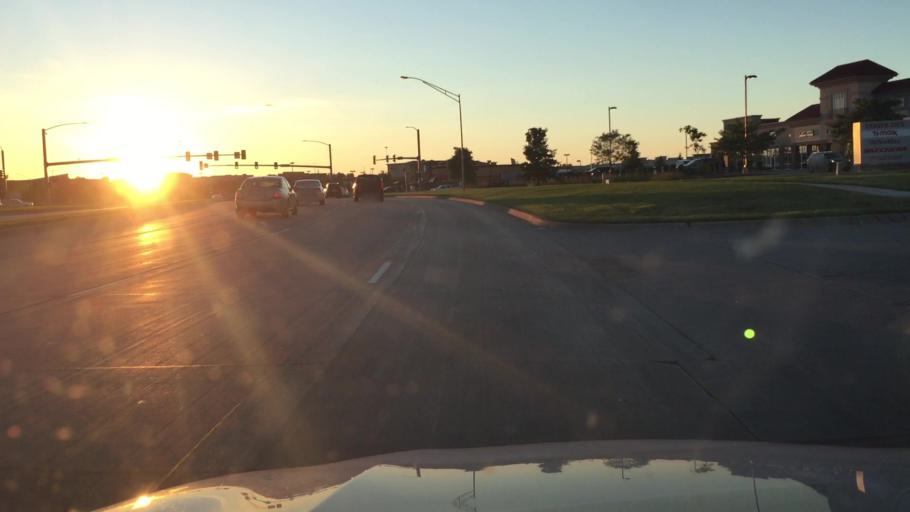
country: US
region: Iowa
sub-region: Polk County
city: Clive
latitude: 41.5608
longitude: -93.7952
